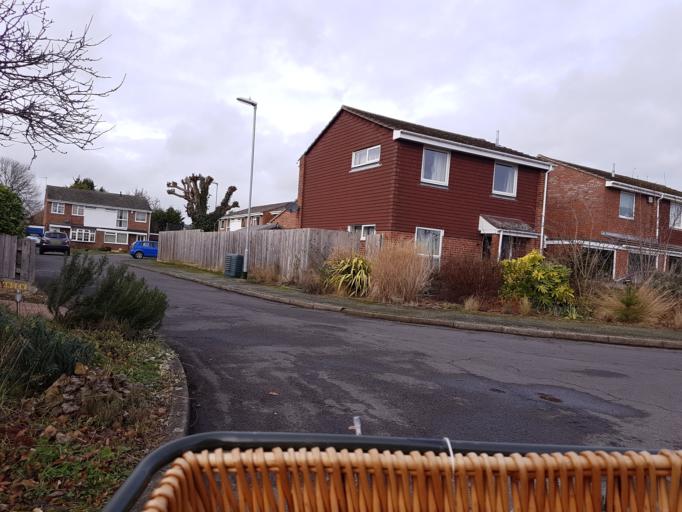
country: GB
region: England
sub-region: Cambridgeshire
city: Girton
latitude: 52.2372
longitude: 0.0866
